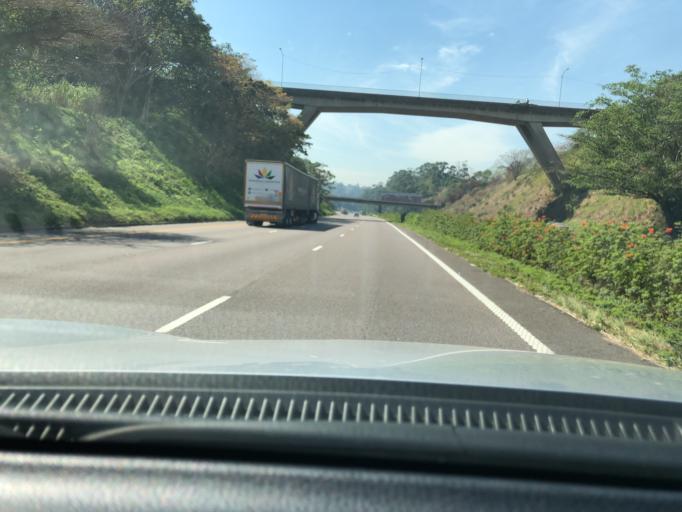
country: ZA
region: KwaZulu-Natal
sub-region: eThekwini Metropolitan Municipality
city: Berea
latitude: -29.8374
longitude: 30.8742
